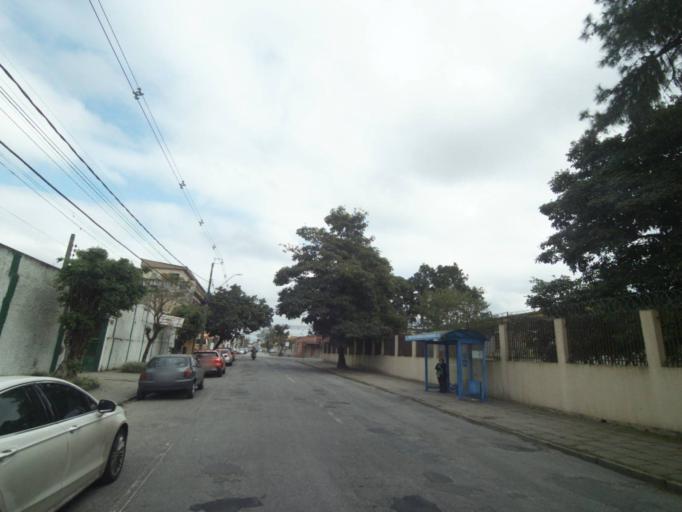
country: BR
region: Parana
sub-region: Paranagua
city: Paranagua
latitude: -25.5233
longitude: -48.5141
